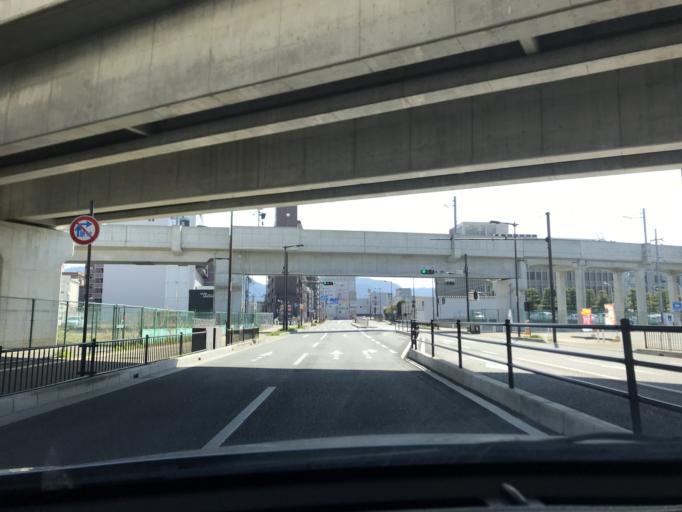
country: JP
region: Nara
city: Nara-shi
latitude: 34.6773
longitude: 135.8169
